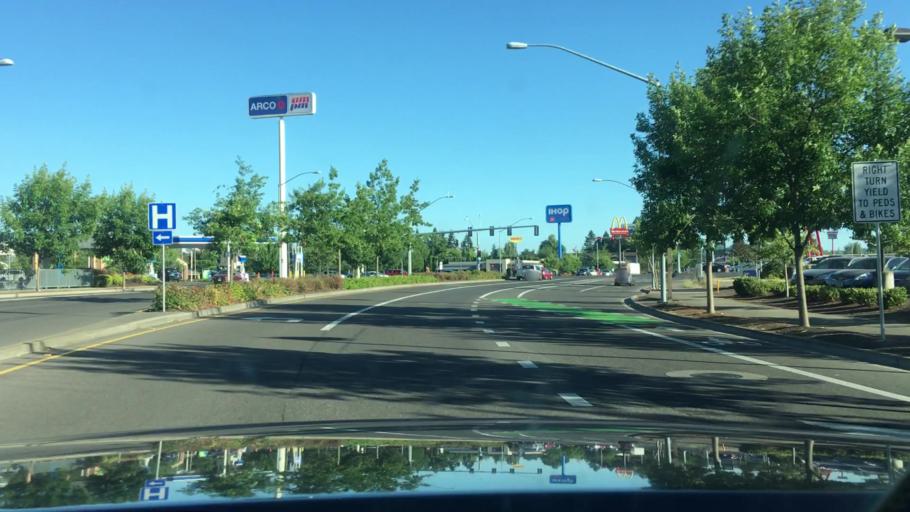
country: US
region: Oregon
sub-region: Lane County
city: Springfield
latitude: 44.0854
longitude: -123.0420
